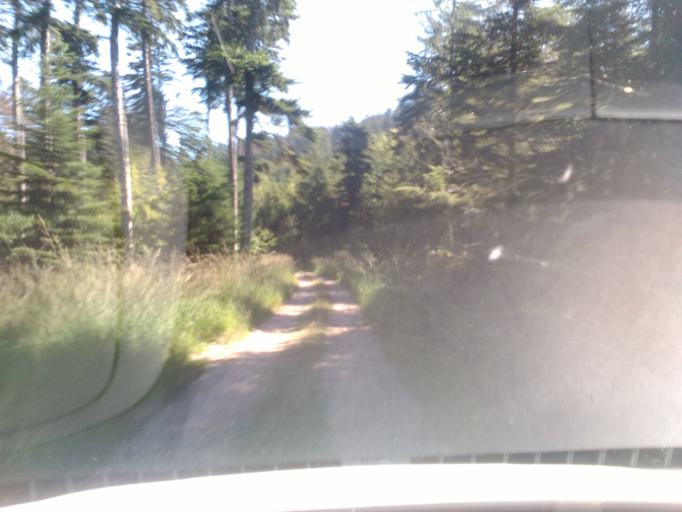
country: FR
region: Lorraine
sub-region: Departement des Vosges
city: Senones
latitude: 48.4305
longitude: 6.9872
